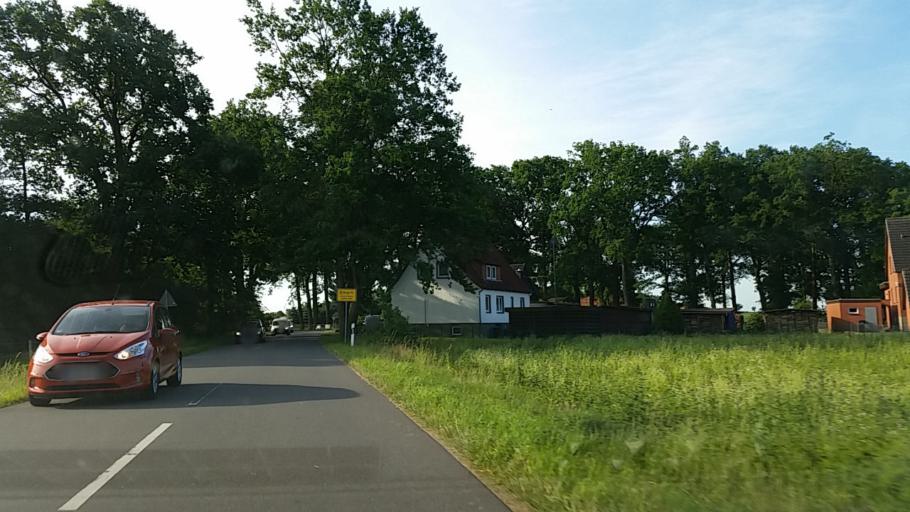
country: DE
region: Lower Saxony
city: Wieren
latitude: 52.9120
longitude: 10.6593
